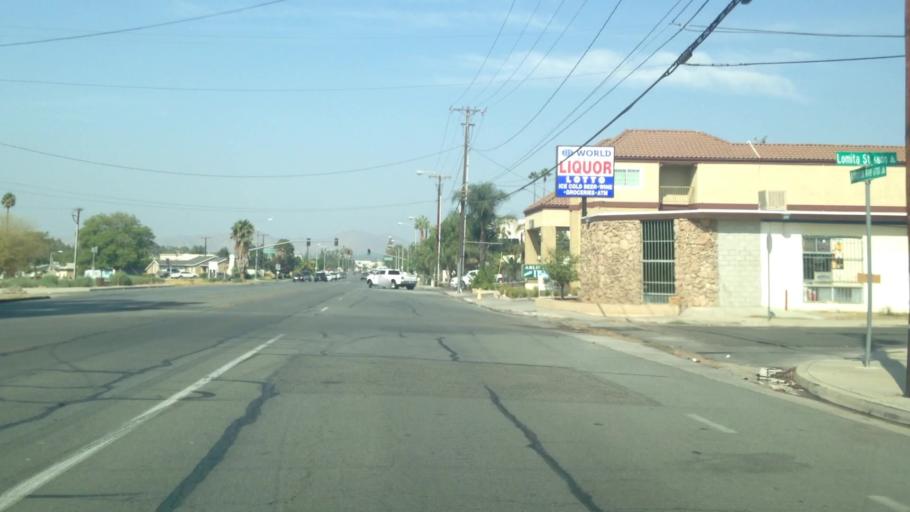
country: US
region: California
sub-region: Riverside County
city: Pedley
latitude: 33.9462
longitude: -117.4437
